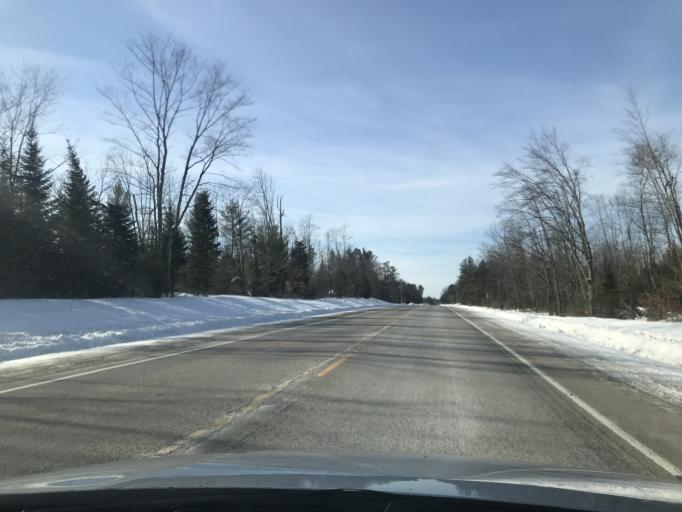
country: US
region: Wisconsin
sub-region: Oconto County
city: Gillett
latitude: 45.1286
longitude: -88.4114
